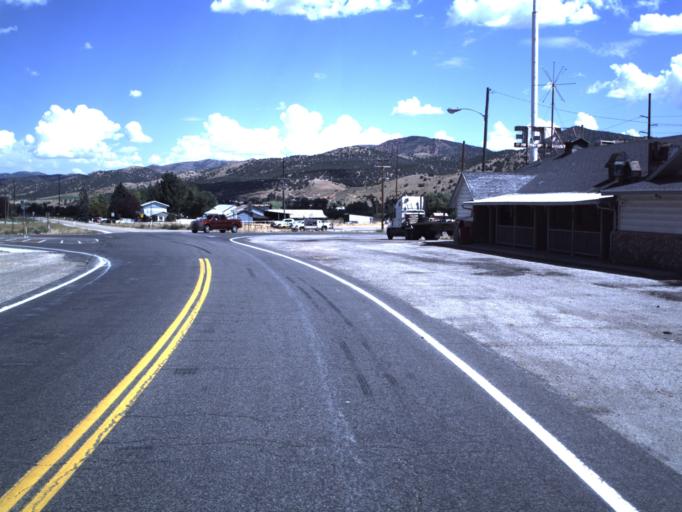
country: US
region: Utah
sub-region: Summit County
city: Coalville
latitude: 40.8125
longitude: -111.4048
